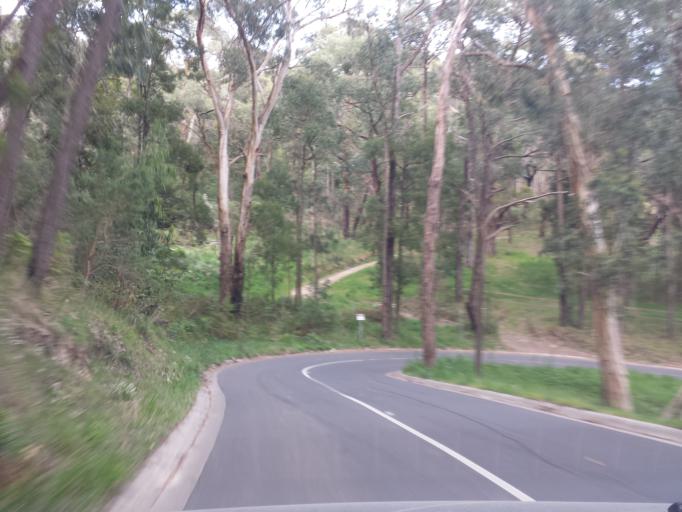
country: AU
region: Victoria
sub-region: Yarra Ranges
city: Kalorama
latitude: -37.8085
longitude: 145.3748
